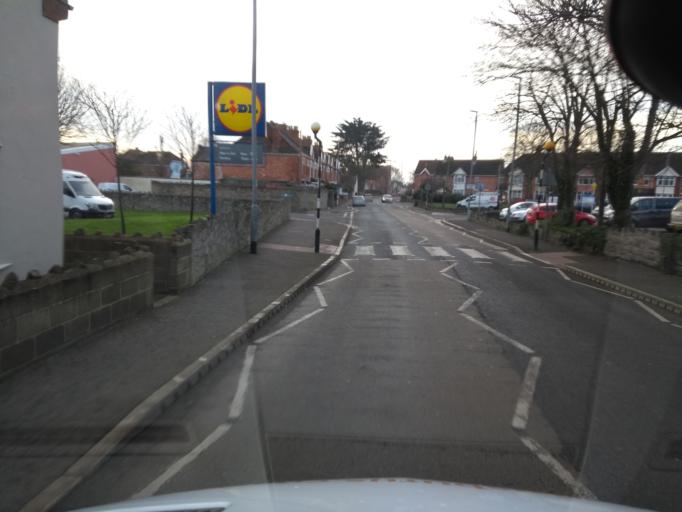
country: GB
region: England
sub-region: Somerset
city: Burnham-on-Sea
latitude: 51.2364
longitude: -2.9951
